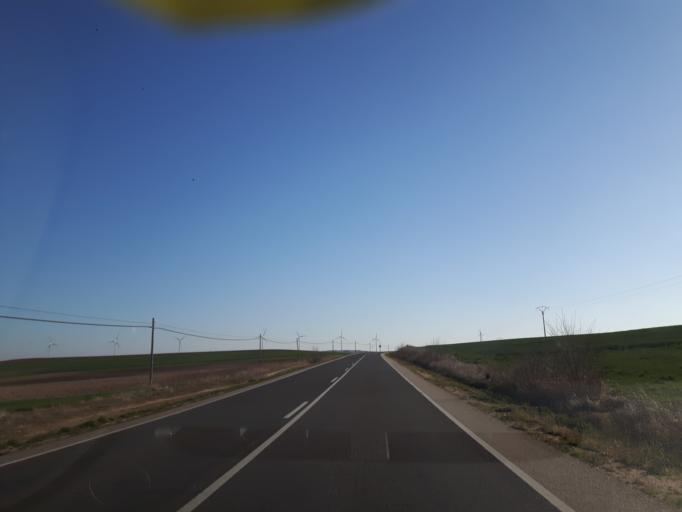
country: ES
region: Castille and Leon
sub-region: Provincia de Salamanca
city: Garcihernandez
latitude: 40.8484
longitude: -5.4567
